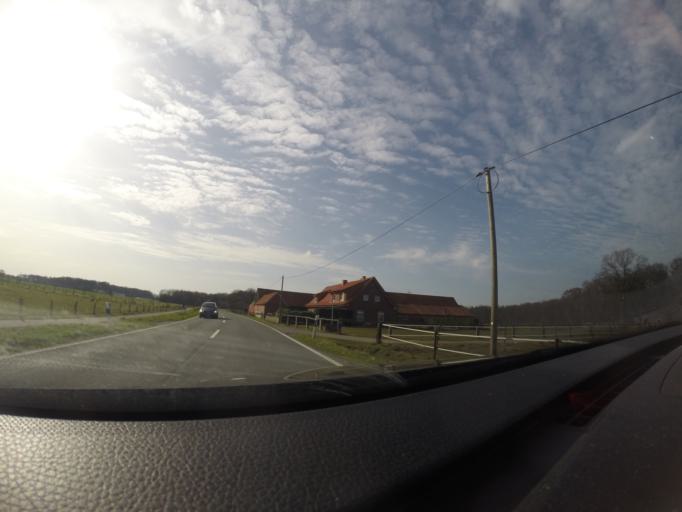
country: DE
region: North Rhine-Westphalia
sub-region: Regierungsbezirk Munster
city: Legden
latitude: 52.0283
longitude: 7.0857
